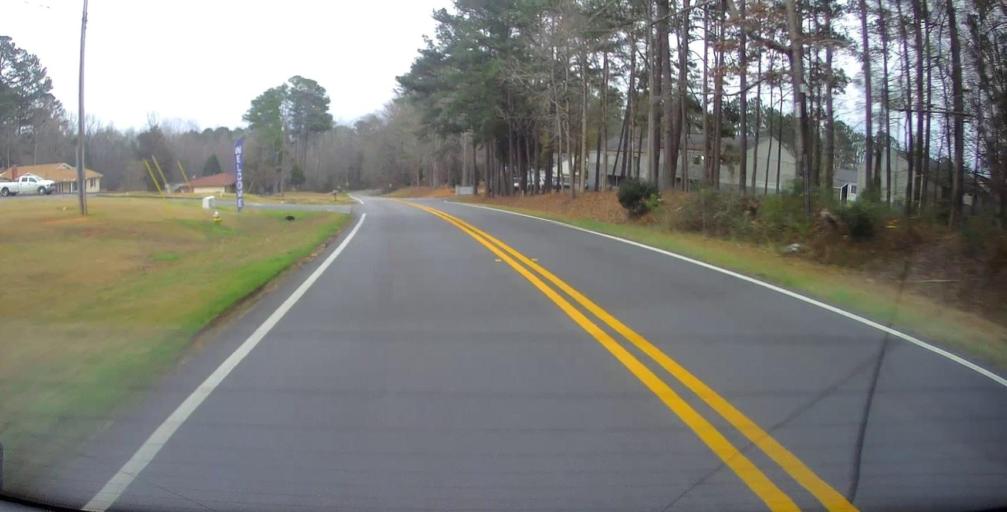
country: US
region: Georgia
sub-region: Bibb County
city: Macon
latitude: 32.9088
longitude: -83.7124
